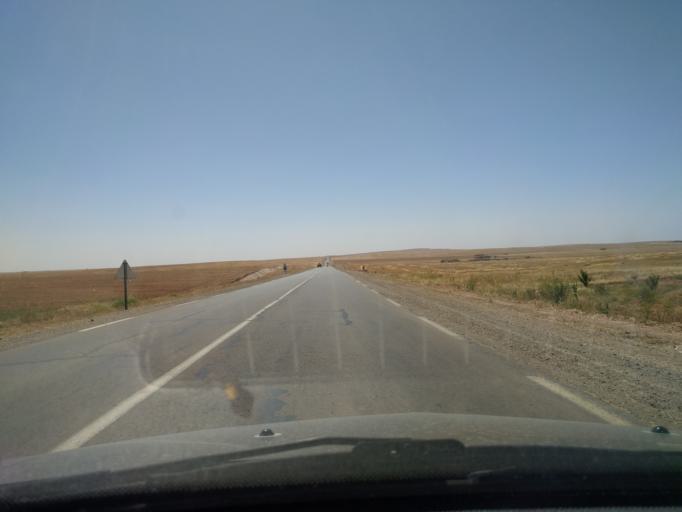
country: DZ
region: Tiaret
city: Frenda
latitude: 34.8913
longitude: 1.1763
